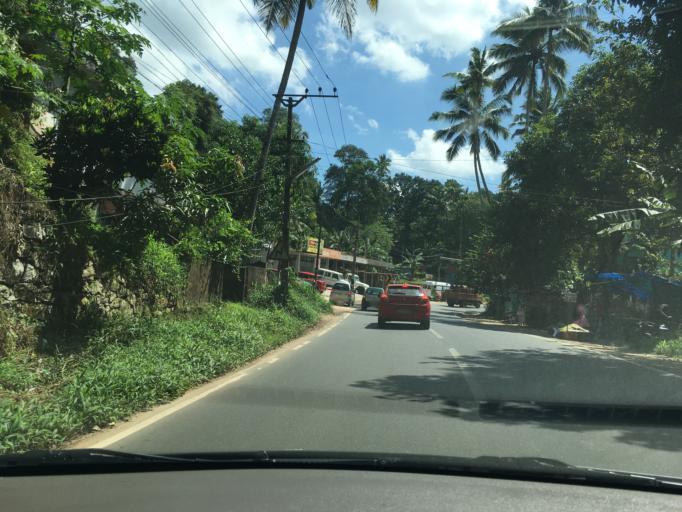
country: IN
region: Kerala
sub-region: Thiruvananthapuram
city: Nedumangad
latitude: 8.5843
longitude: 76.9961
